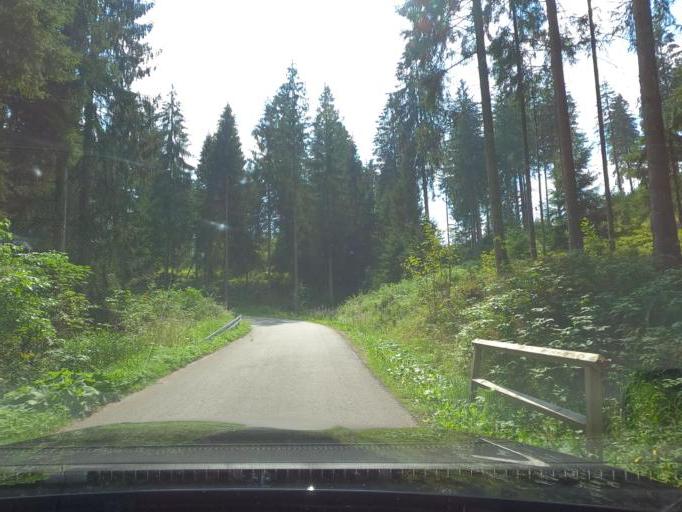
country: DE
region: Lower Saxony
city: Clausthal-Zellerfeld
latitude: 51.7762
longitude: 10.3050
